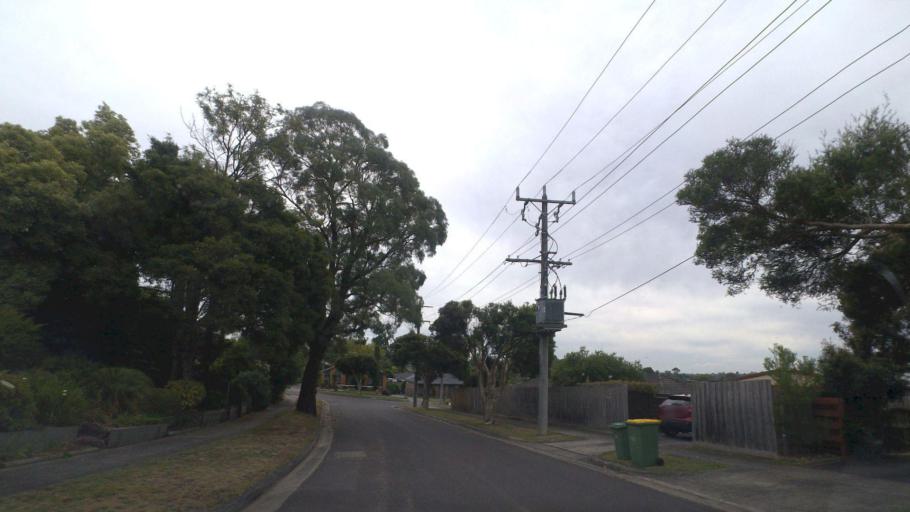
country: AU
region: Victoria
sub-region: Yarra Ranges
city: Kilsyth
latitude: -37.7986
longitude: 145.3305
